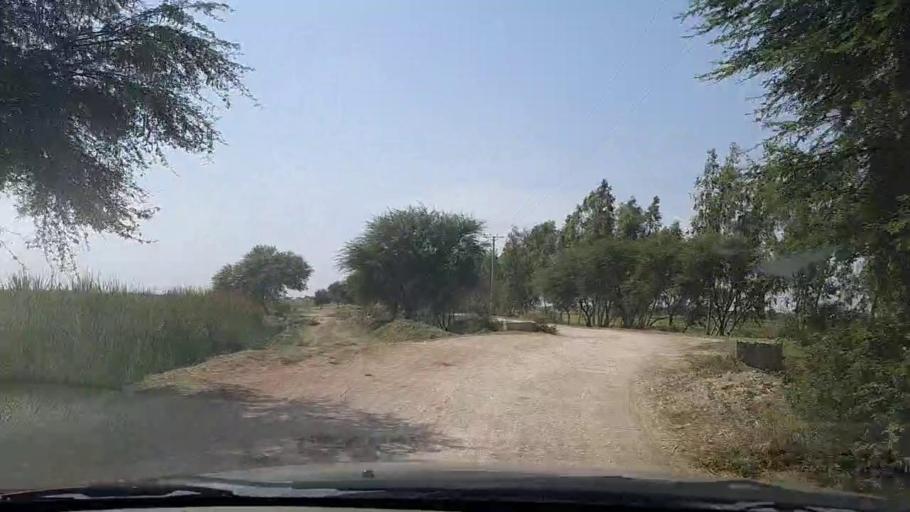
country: PK
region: Sindh
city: Mirpur Batoro
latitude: 24.6105
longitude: 68.2392
